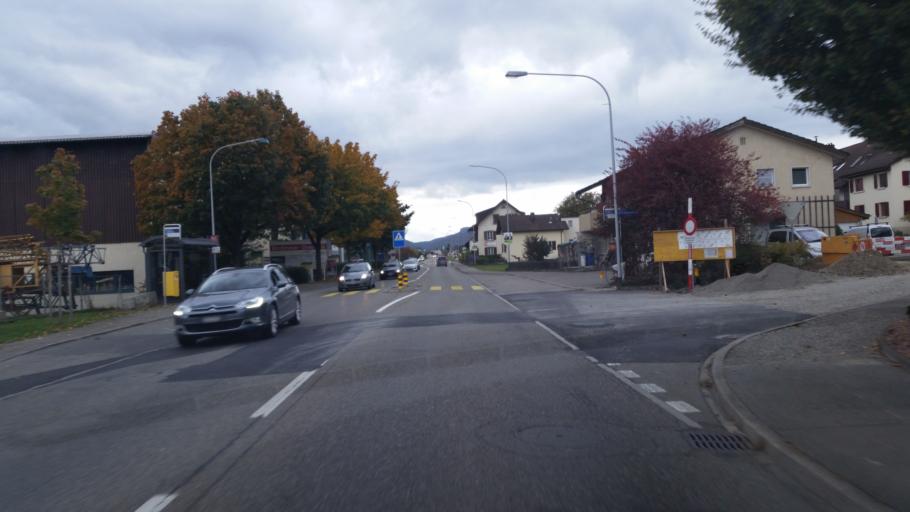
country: CH
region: Aargau
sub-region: Bezirk Baden
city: Obersiggenthal
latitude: 47.4933
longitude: 8.2764
